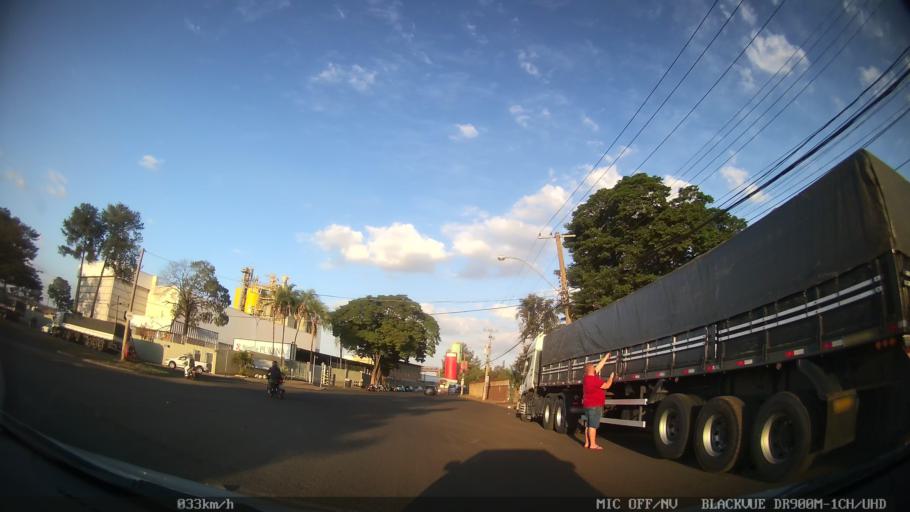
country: BR
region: Sao Paulo
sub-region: Ribeirao Preto
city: Ribeirao Preto
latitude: -21.1447
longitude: -47.7850
